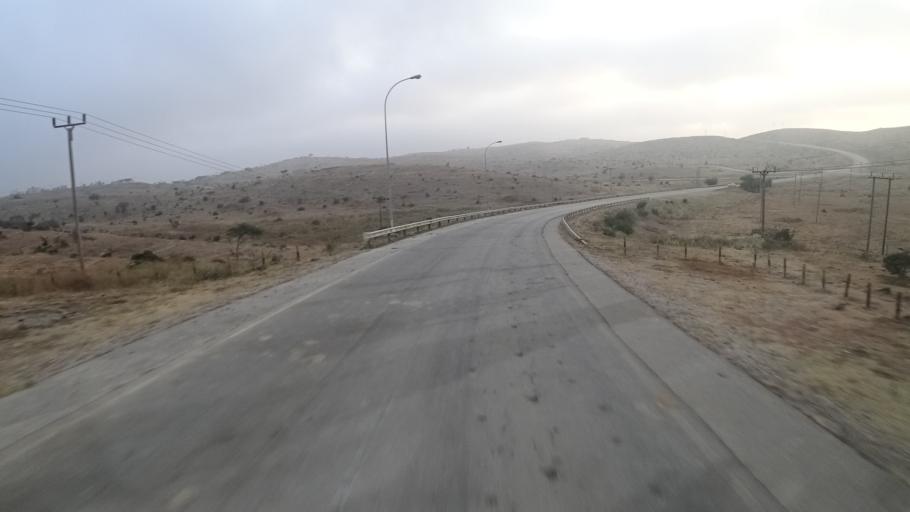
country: OM
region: Zufar
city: Salalah
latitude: 17.1295
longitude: 53.9614
